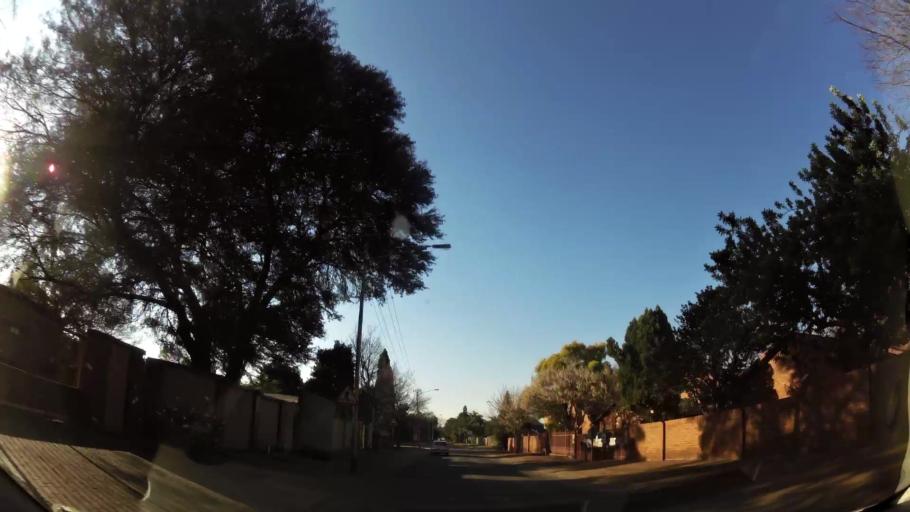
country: ZA
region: Gauteng
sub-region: City of Tshwane Metropolitan Municipality
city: Centurion
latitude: -25.8668
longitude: 28.1500
